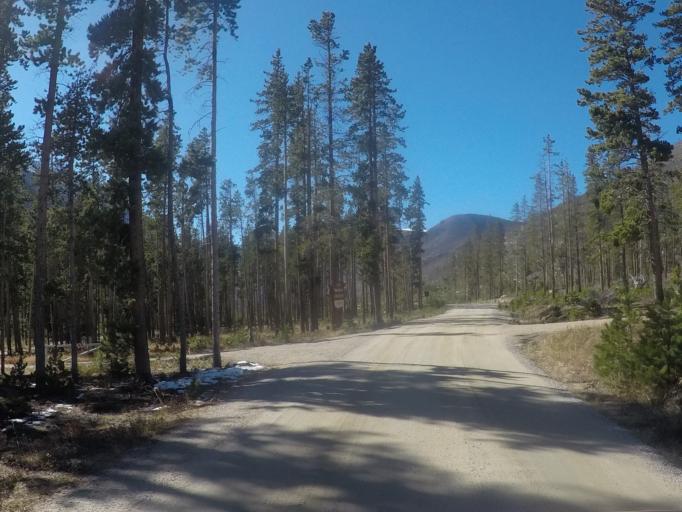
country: US
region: Montana
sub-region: Carbon County
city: Red Lodge
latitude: 45.1733
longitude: -109.4505
